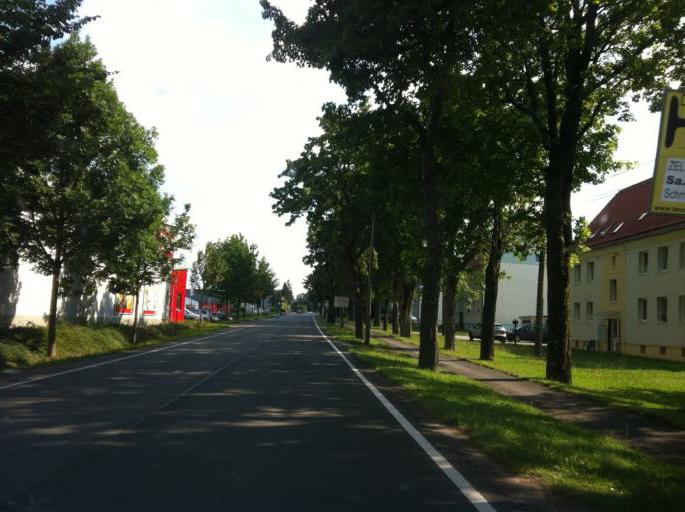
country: DE
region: Thuringia
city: Grossbreitenbach
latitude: 50.5844
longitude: 10.9950
